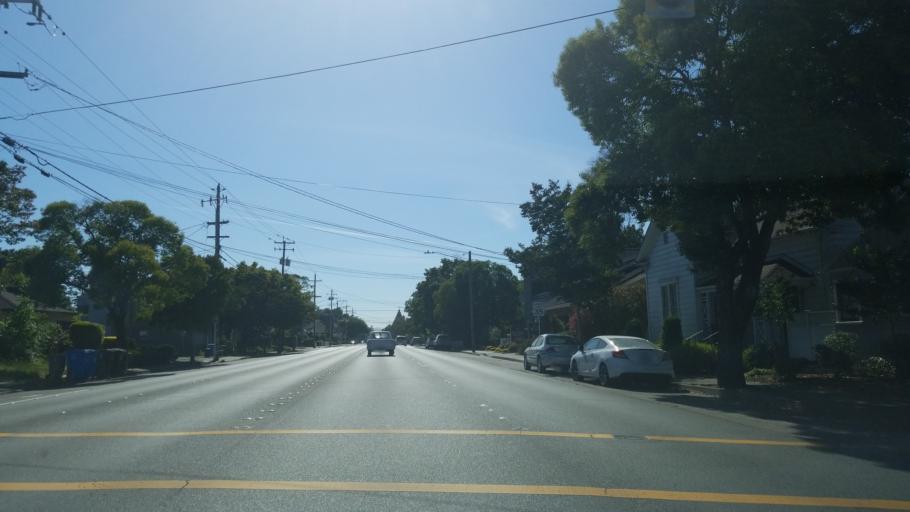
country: US
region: California
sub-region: Sonoma County
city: Santa Rosa
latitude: 38.4455
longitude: -122.7109
